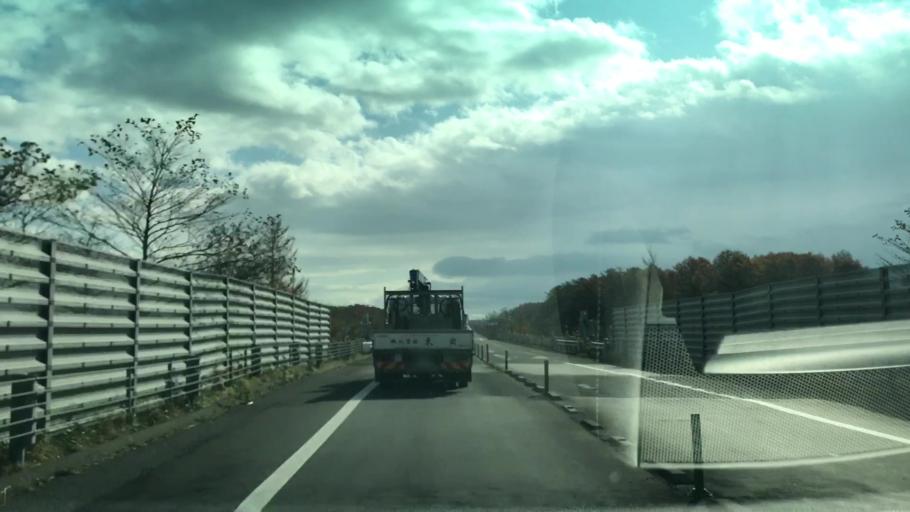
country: JP
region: Hokkaido
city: Tomakomai
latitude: 42.5704
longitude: 141.9754
